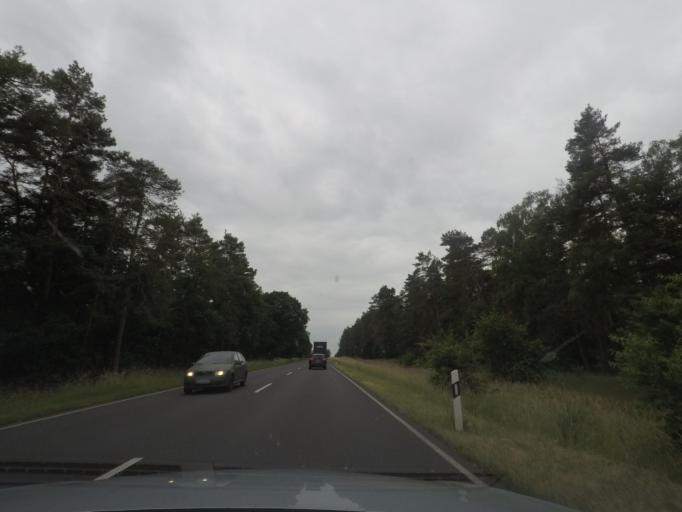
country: DE
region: Saxony-Anhalt
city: Haldensleben I
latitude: 52.3313
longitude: 11.4458
